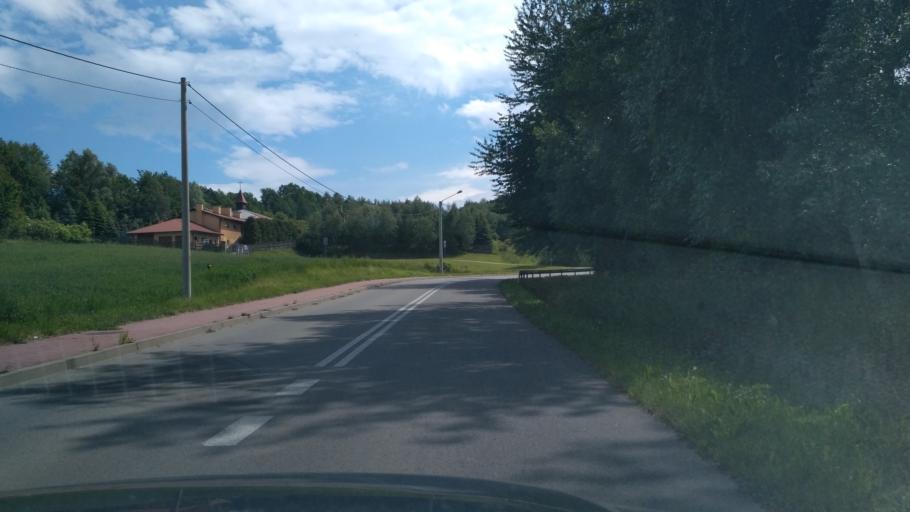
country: PL
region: Subcarpathian Voivodeship
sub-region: Powiat ropczycko-sedziszowski
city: Ropczyce
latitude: 50.0484
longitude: 21.6219
